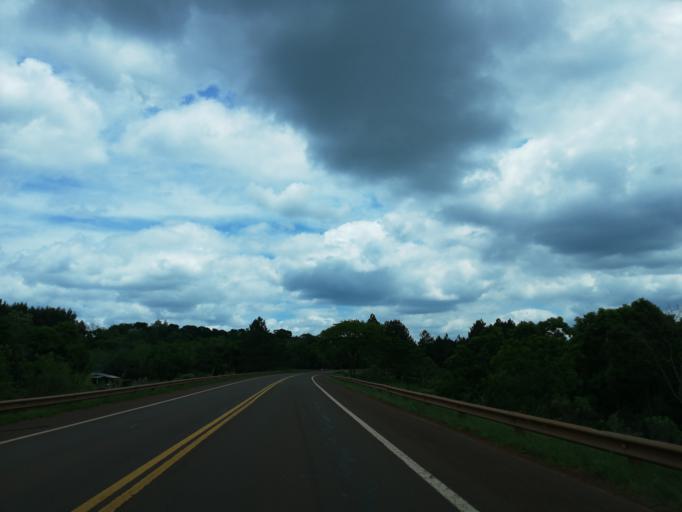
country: AR
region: Misiones
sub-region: Departamento de Leandro N. Alem
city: Leandro N. Alem
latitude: -27.6454
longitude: -55.3548
